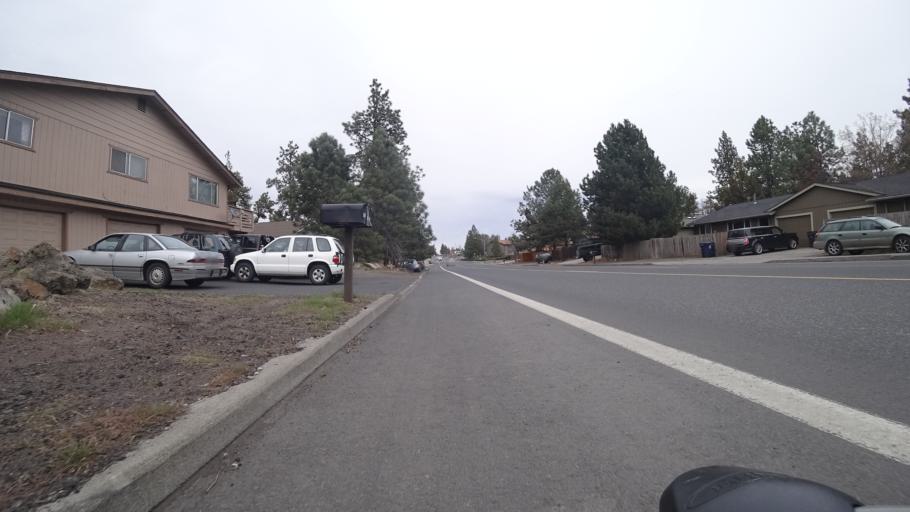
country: US
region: Oregon
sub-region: Deschutes County
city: Bend
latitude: 44.0444
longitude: -121.2967
